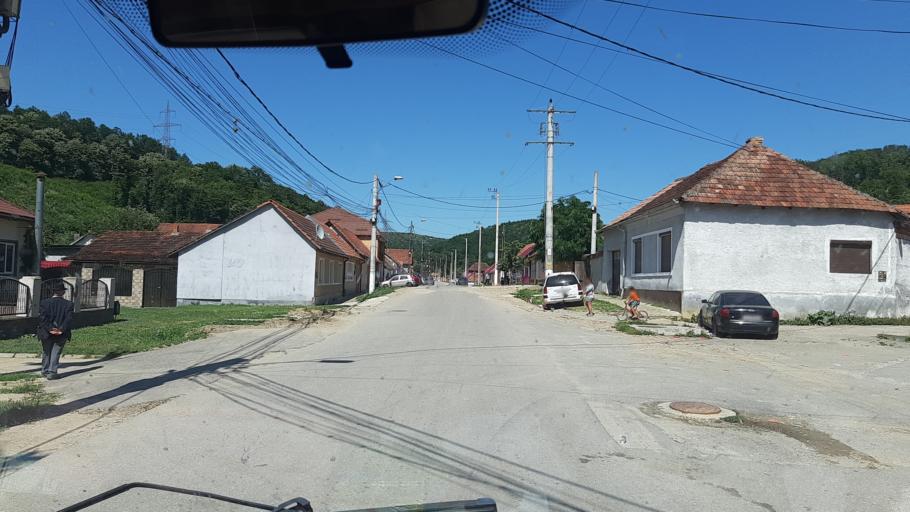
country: RO
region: Caras-Severin
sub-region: Municipiul Resita
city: Calnic
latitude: 45.3859
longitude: 21.7976
